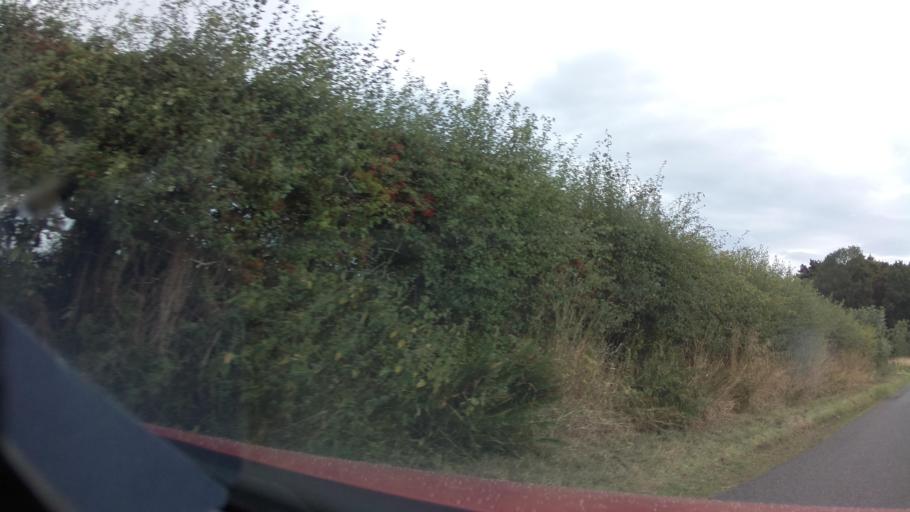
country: GB
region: Scotland
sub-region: Fife
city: Saint Andrews
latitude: 56.2995
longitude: -2.7894
